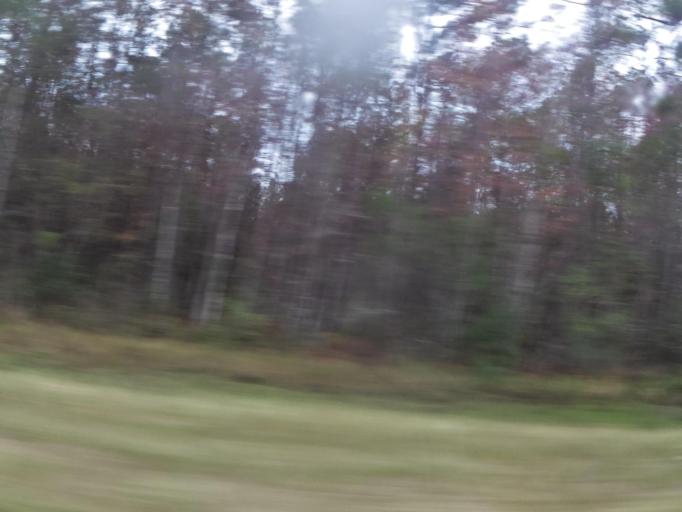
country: US
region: Georgia
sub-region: Charlton County
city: Folkston
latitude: 30.8950
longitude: -82.0547
